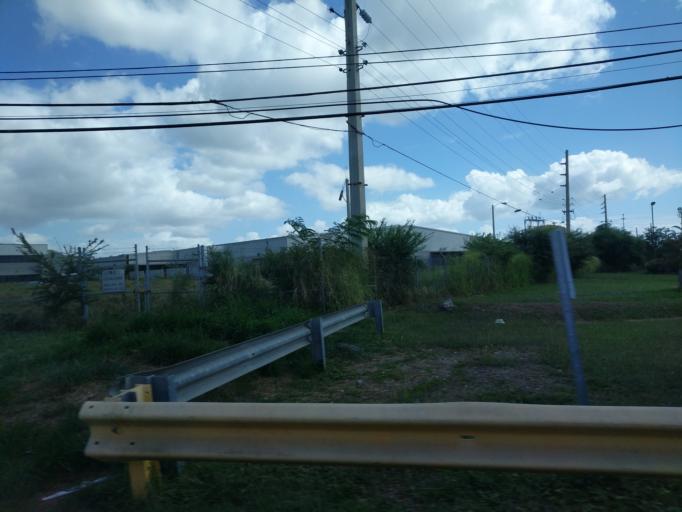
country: PR
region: Santa Isabel Municipio
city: El Ojo
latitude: 18.0136
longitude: -66.3834
